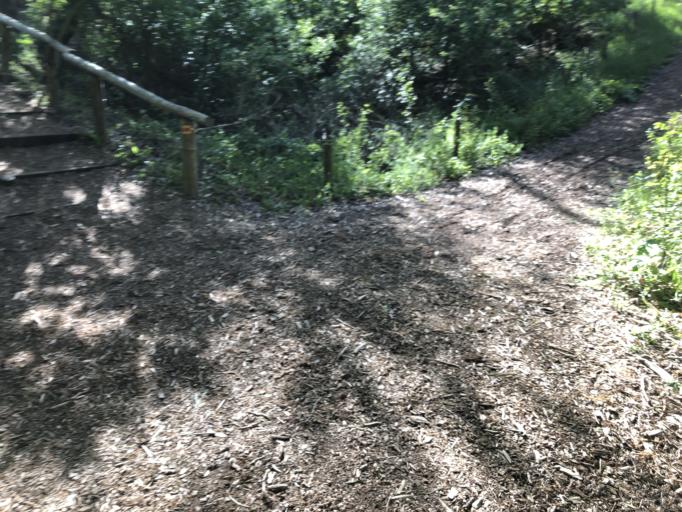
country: NL
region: South Holland
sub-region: Gemeente Wassenaar
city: Wassenaar
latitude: 52.1733
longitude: 4.3928
